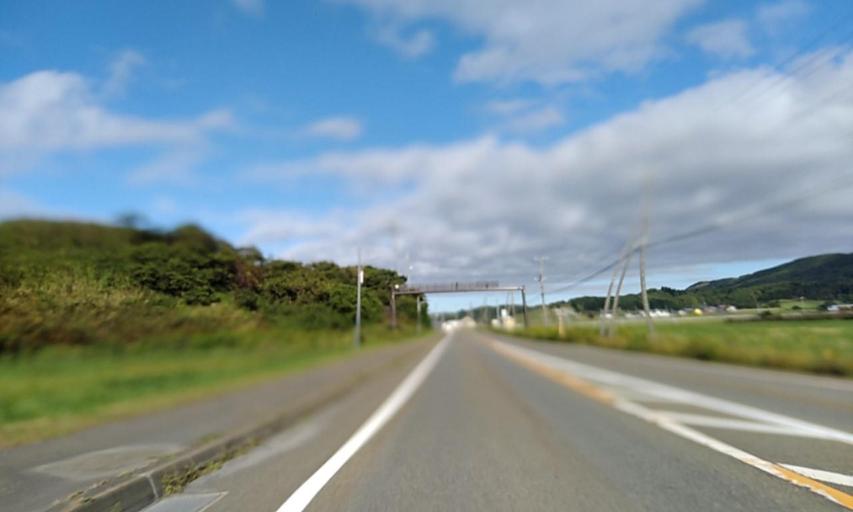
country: JP
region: Hokkaido
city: Shizunai-furukawacho
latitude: 42.2220
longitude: 142.6332
